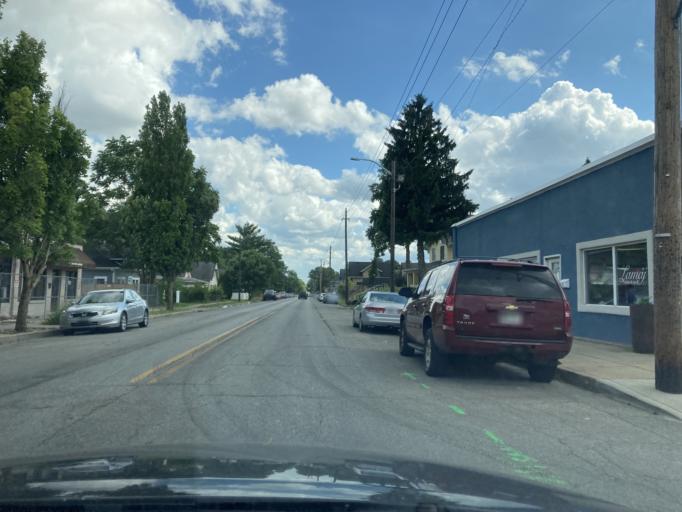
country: US
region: Indiana
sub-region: Marion County
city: Broad Ripple
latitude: 39.8283
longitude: -86.1640
